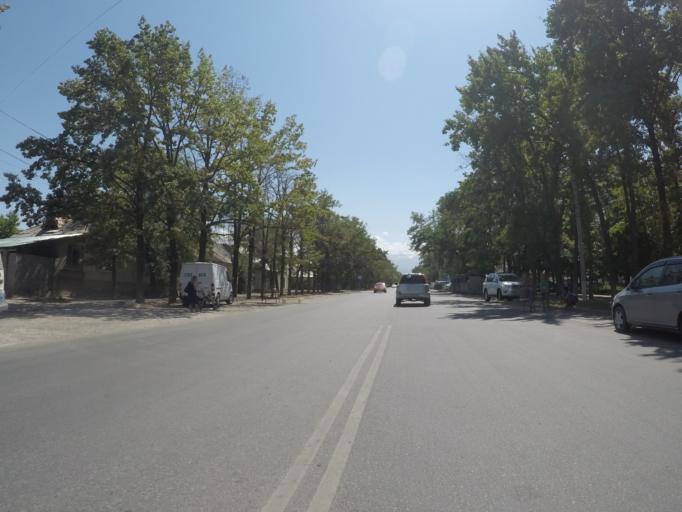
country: KG
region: Chuy
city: Bishkek
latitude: 42.8475
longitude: 74.5769
